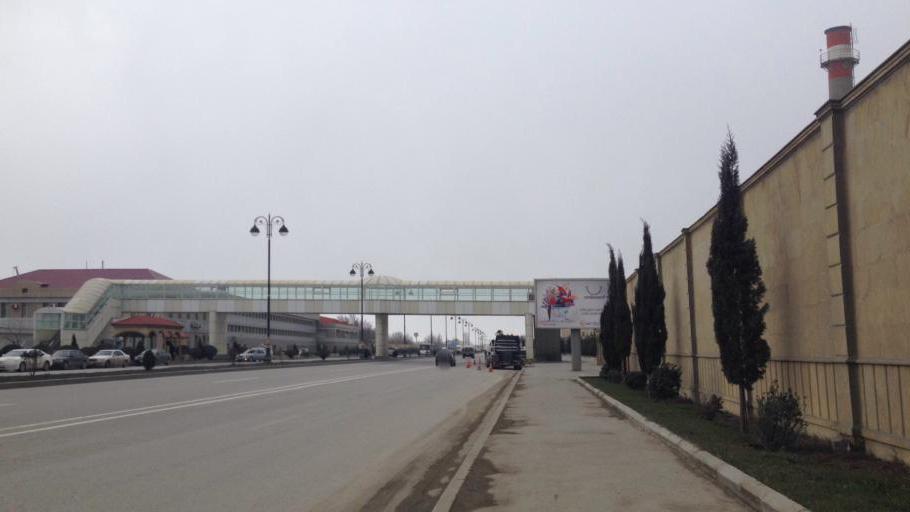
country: AZ
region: Baki
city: Baku
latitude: 40.3771
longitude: 49.9084
